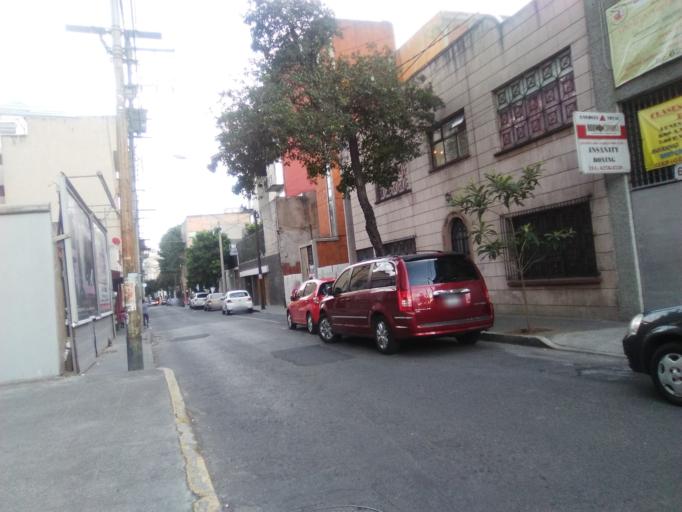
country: MX
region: Mexico City
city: Alvaro Obregon
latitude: 19.3761
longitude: -99.1865
